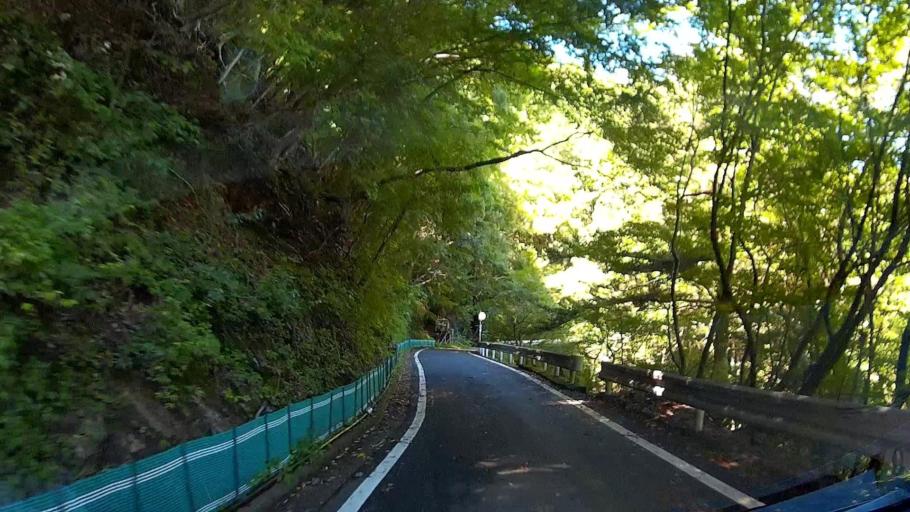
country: JP
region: Shizuoka
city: Shizuoka-shi
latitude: 35.1932
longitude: 138.2635
